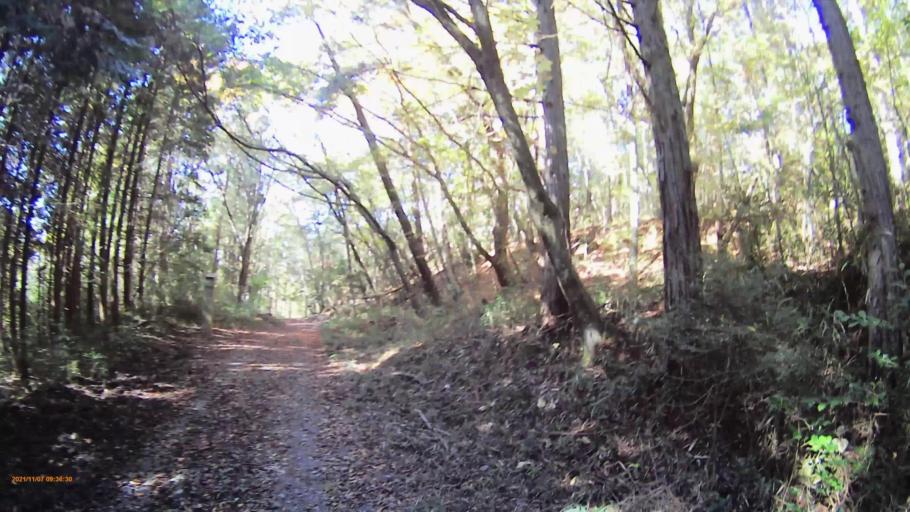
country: JP
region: Gifu
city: Mizunami
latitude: 35.4460
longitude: 137.3459
